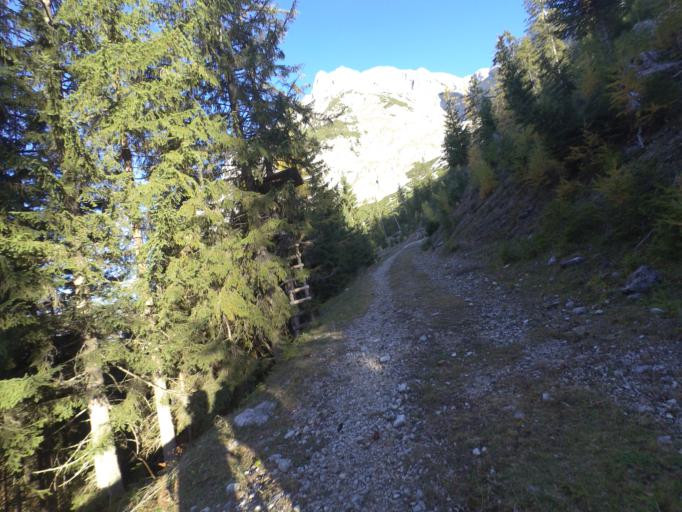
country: AT
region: Salzburg
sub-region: Politischer Bezirk Sankt Johann im Pongau
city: Werfenweng
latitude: 47.4860
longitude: 13.2297
